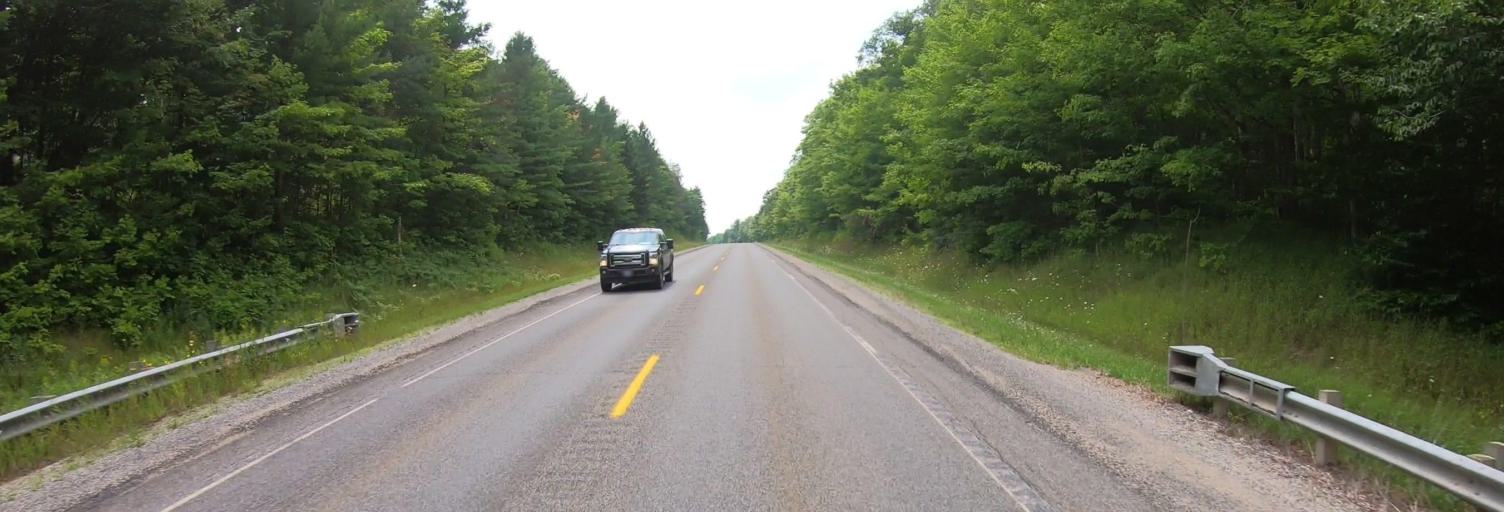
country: US
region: Michigan
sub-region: Alger County
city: Munising
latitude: 46.3586
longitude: -86.7182
